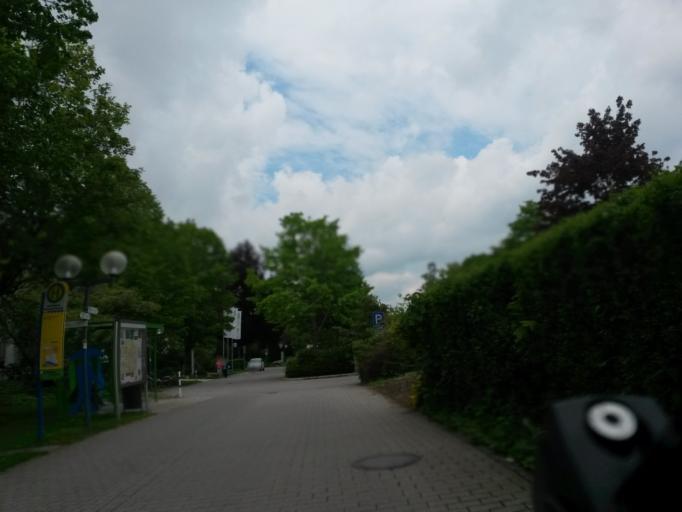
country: DE
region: Baden-Wuerttemberg
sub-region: Tuebingen Region
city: Bad Waldsee
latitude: 47.9157
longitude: 9.7630
